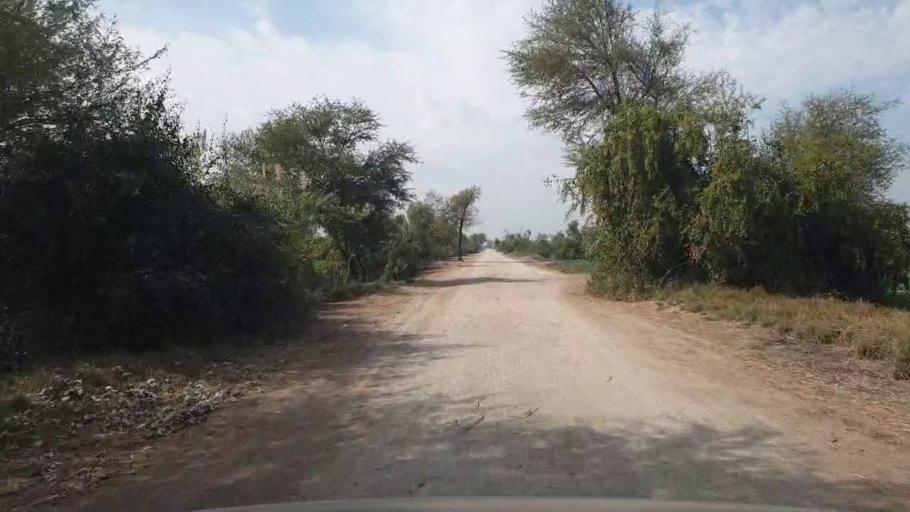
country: PK
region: Sindh
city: Sakrand
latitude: 25.9976
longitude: 68.3899
